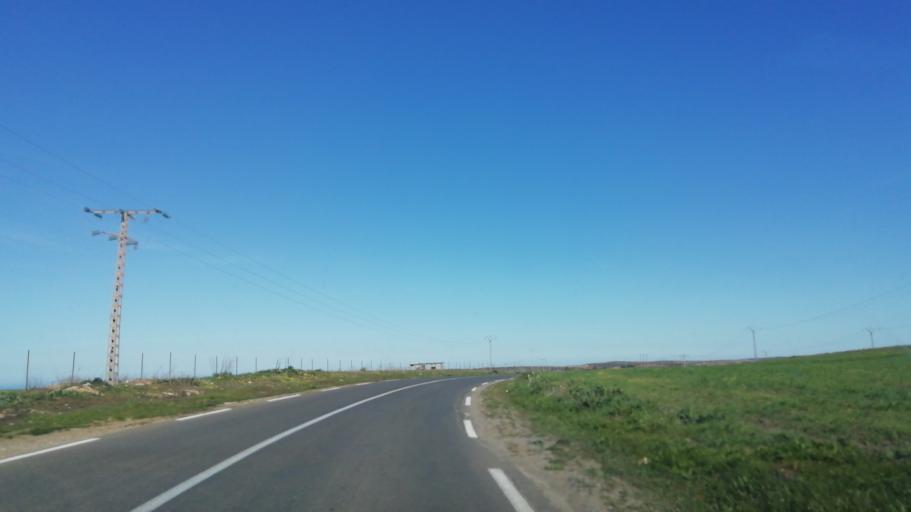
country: DZ
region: Oran
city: Bou Tlelis
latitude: 35.6448
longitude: -0.9459
